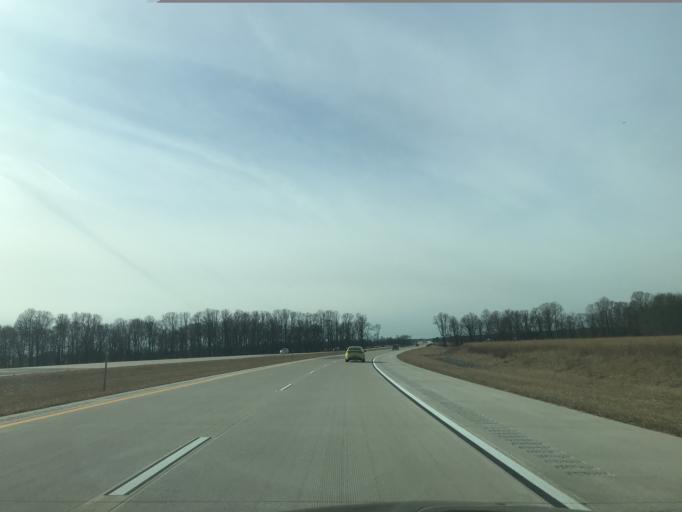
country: US
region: Delaware
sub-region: New Castle County
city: Middletown
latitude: 39.4991
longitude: -75.6973
